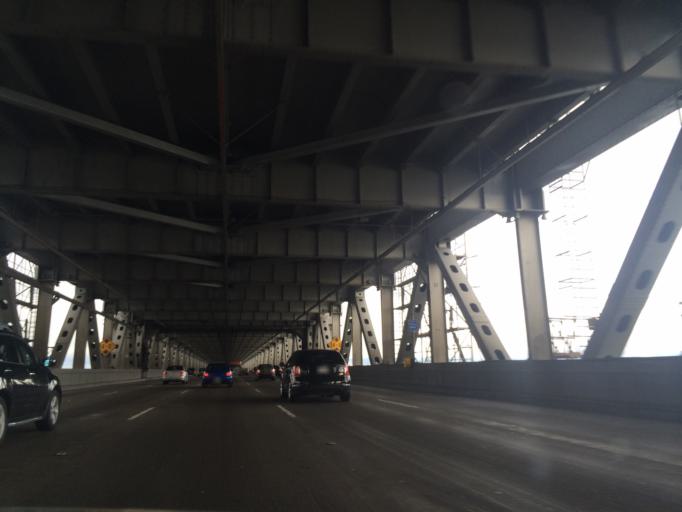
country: US
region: California
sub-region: San Francisco County
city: San Francisco
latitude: 37.7945
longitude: -122.3818
